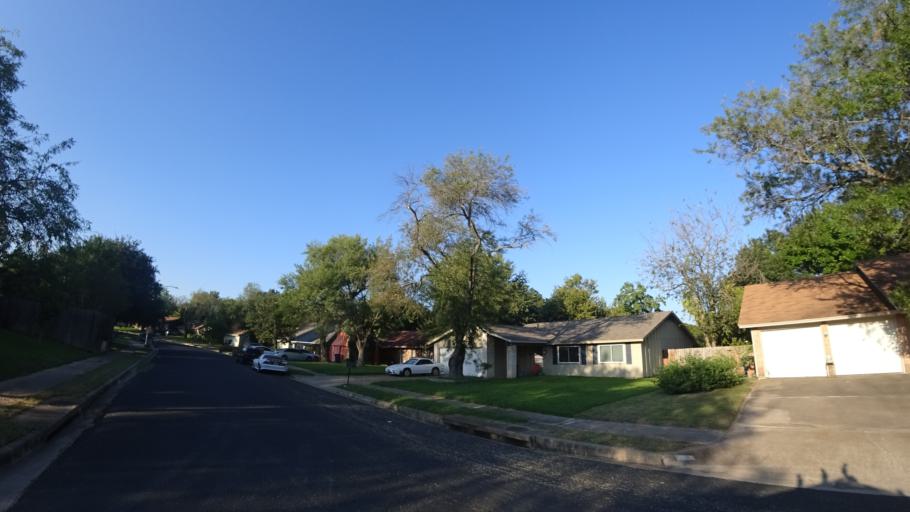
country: US
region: Texas
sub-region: Travis County
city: Wells Branch
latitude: 30.3600
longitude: -97.6742
